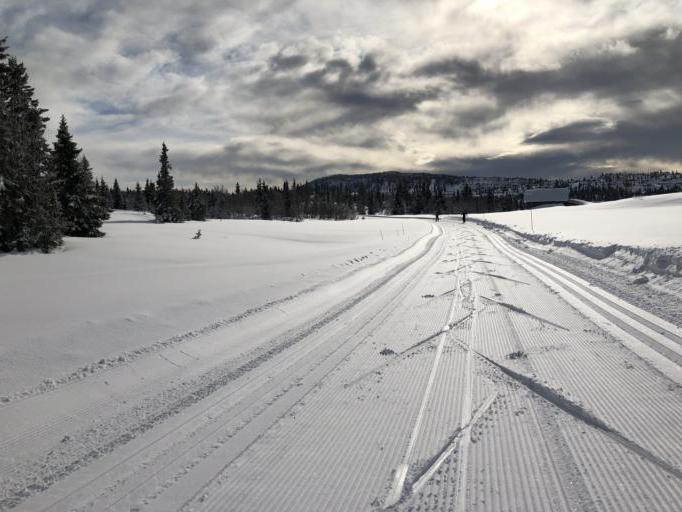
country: NO
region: Oppland
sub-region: Gausdal
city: Segalstad bru
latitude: 61.3173
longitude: 10.0600
